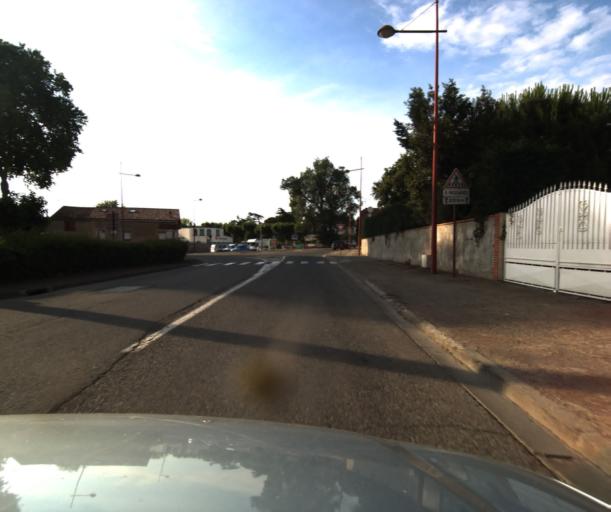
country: FR
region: Midi-Pyrenees
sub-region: Departement du Tarn-et-Garonne
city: Castelsarrasin
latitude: 44.0350
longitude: 1.1060
